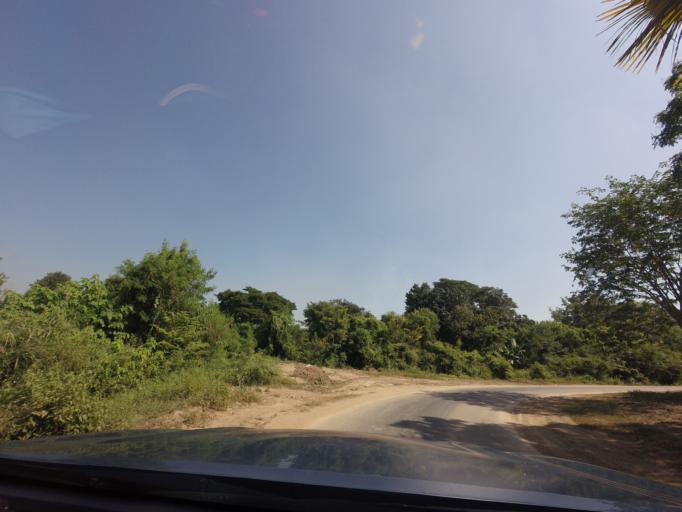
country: TH
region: Sukhothai
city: Sawankhalok
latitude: 17.2767
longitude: 99.8227
